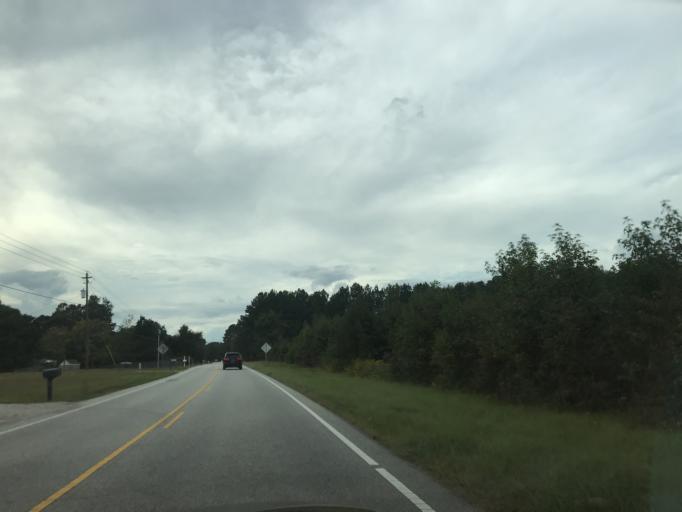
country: US
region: North Carolina
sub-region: Franklin County
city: Youngsville
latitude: 35.9976
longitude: -78.4181
